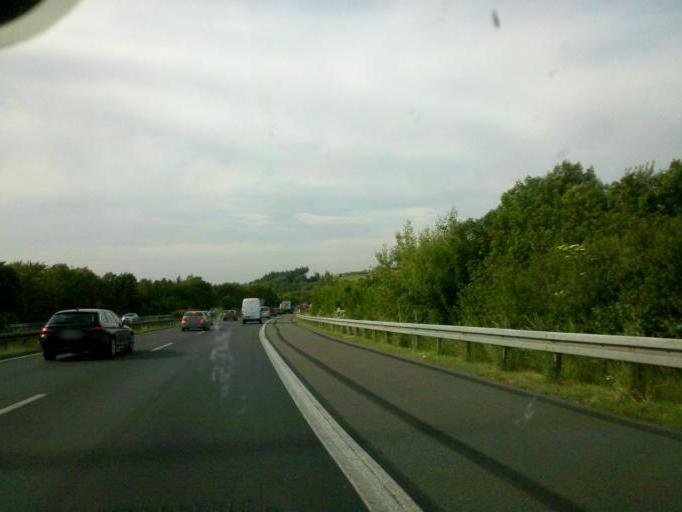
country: DE
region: North Rhine-Westphalia
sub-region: Regierungsbezirk Arnsberg
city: Schalksmuhle
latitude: 51.2956
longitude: 7.5537
